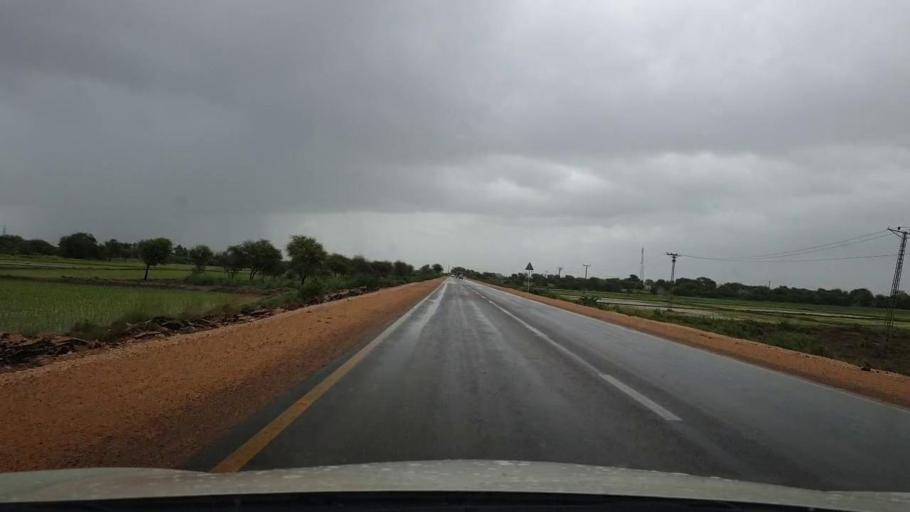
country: PK
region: Sindh
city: Kario
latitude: 24.6527
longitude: 68.6557
